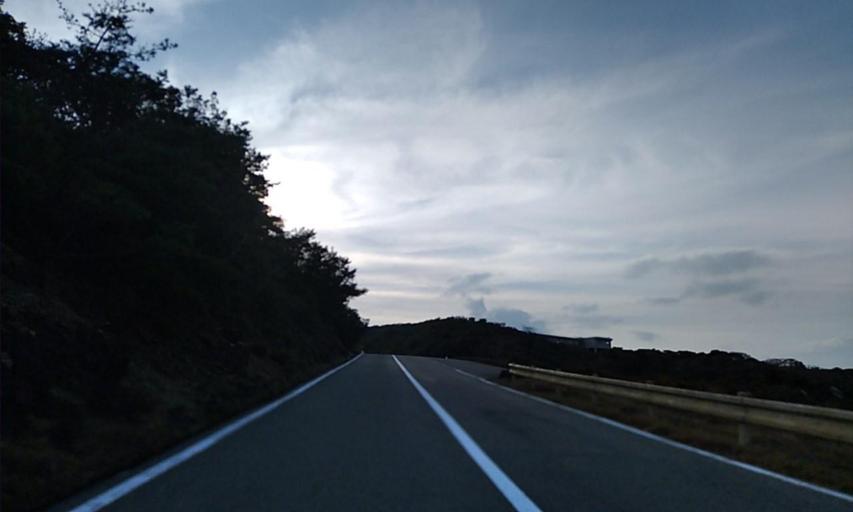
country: JP
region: Mie
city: Toba
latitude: 34.4601
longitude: 136.7945
